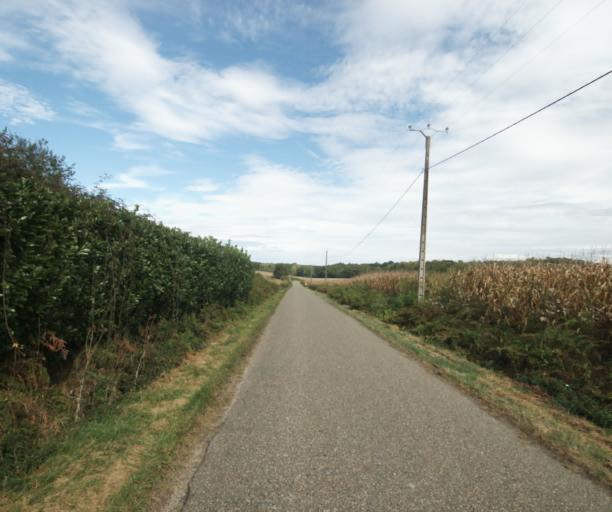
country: FR
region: Aquitaine
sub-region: Departement des Landes
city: Villeneuve-de-Marsan
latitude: 43.8986
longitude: -0.2280
